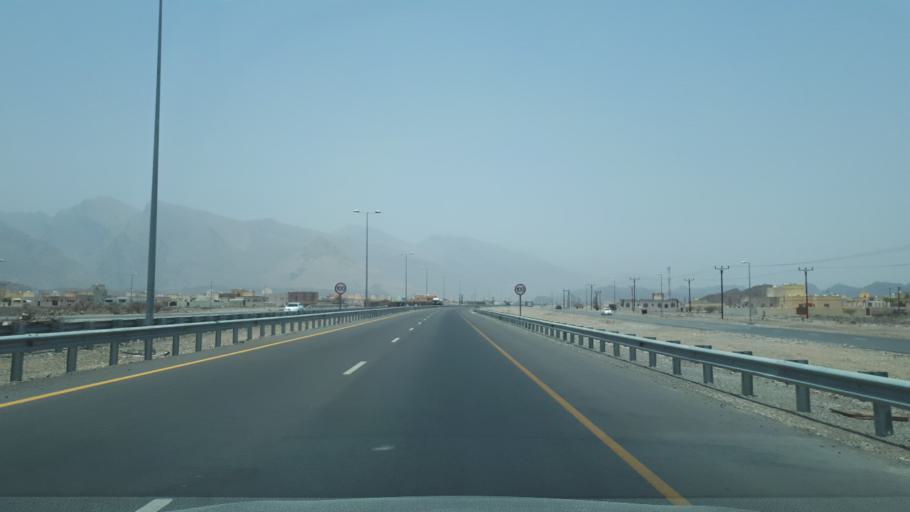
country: OM
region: Al Batinah
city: Rustaq
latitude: 23.4219
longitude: 57.3710
